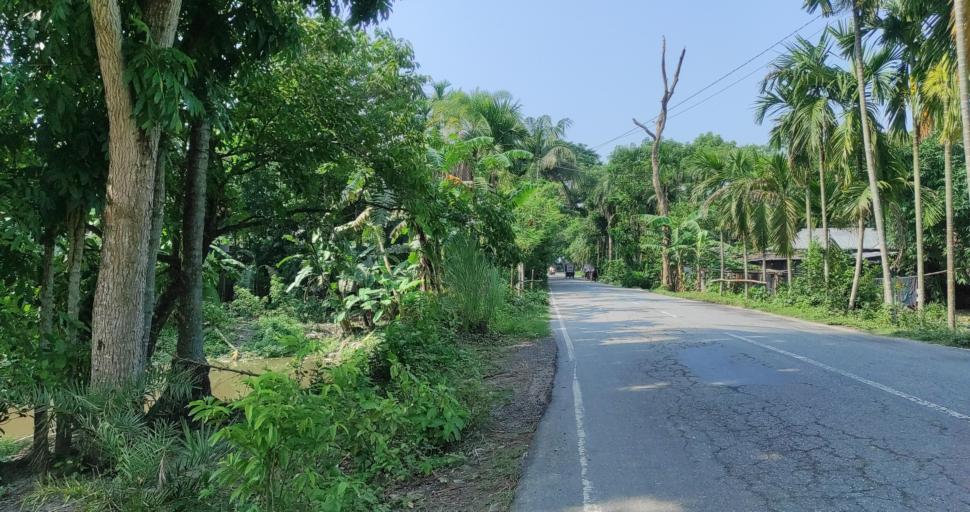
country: BD
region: Rajshahi
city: Ishurdi
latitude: 24.2819
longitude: 89.0645
